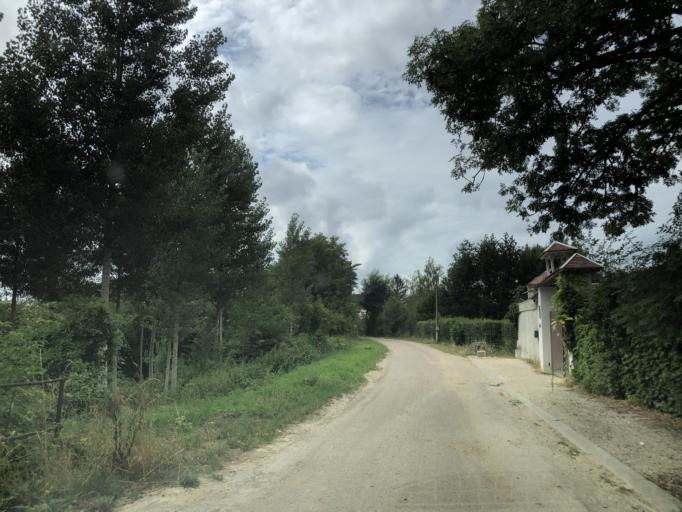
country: FR
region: Bourgogne
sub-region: Departement de l'Yonne
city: Laroche-Saint-Cydroine
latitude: 47.9471
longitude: 3.4488
